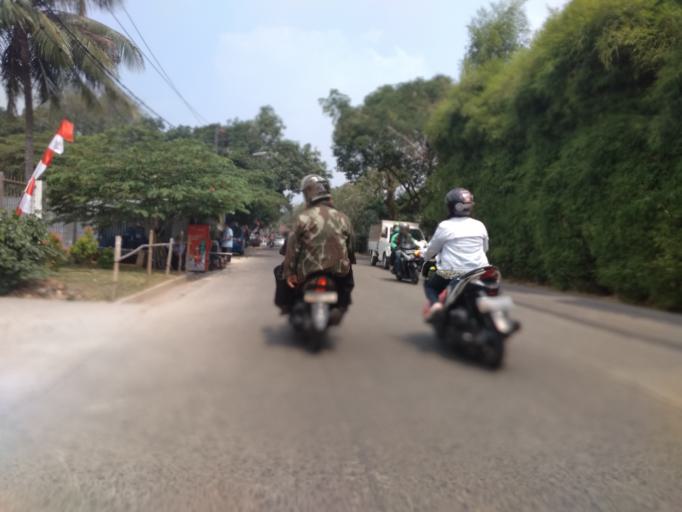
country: ID
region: West Java
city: Pamulang
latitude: -6.3184
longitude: 106.7891
